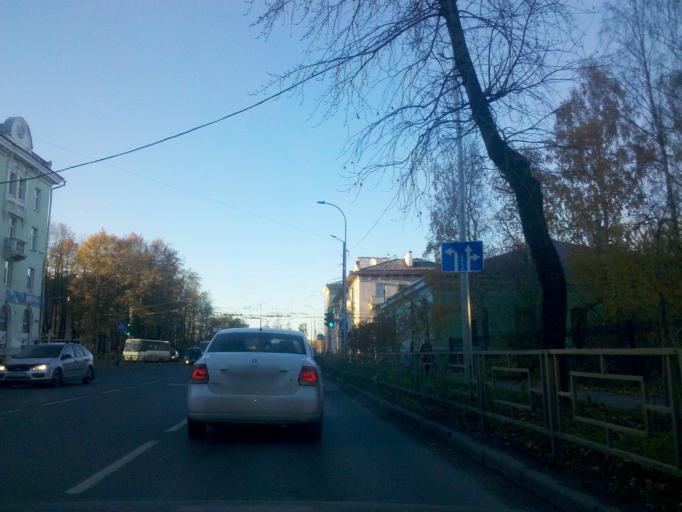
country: RU
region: Republic of Karelia
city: Petrozavodsk
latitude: 61.7815
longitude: 34.3871
